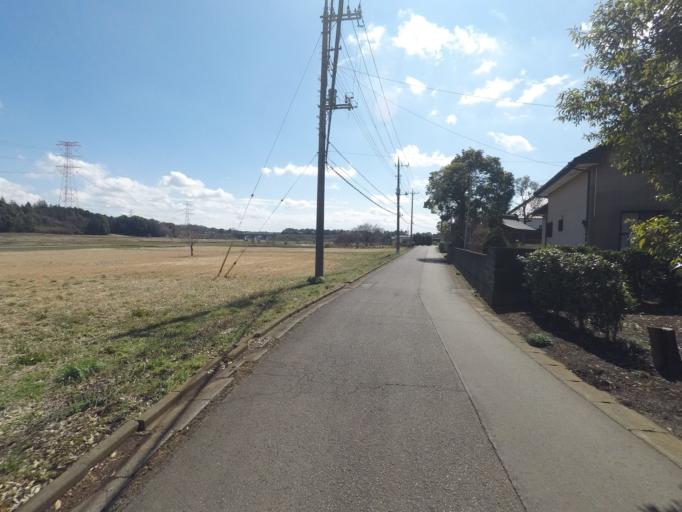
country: JP
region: Ibaraki
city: Mitsukaido
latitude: 36.0243
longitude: 140.0681
